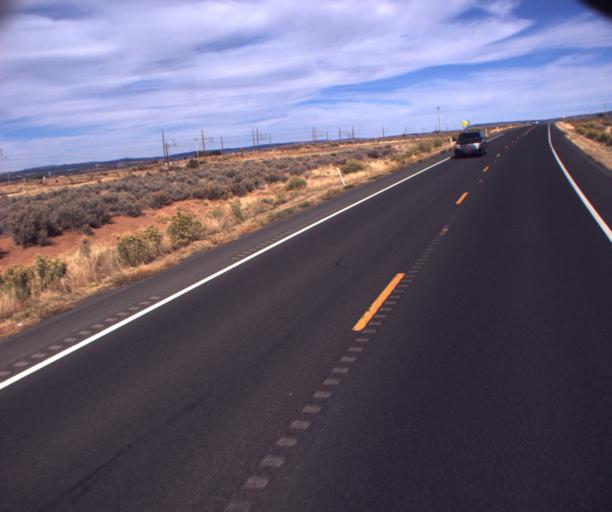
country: US
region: Arizona
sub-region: Navajo County
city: Kayenta
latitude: 36.5178
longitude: -110.5920
